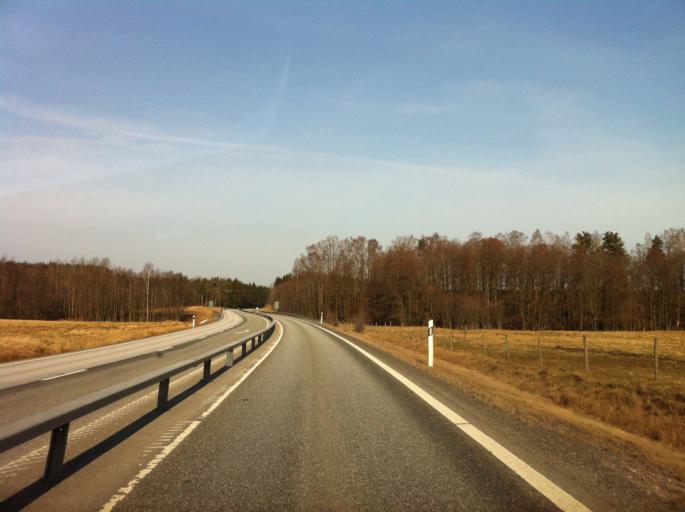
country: SE
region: Joenkoeping
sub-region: Jonkopings Kommun
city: Bankeryd
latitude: 57.8440
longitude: 14.1072
